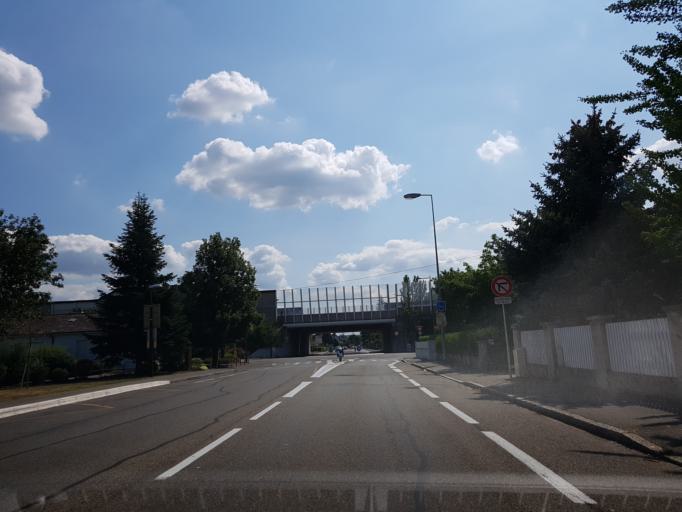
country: FR
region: Alsace
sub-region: Departement du Haut-Rhin
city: Illzach
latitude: 47.7747
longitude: 7.3617
